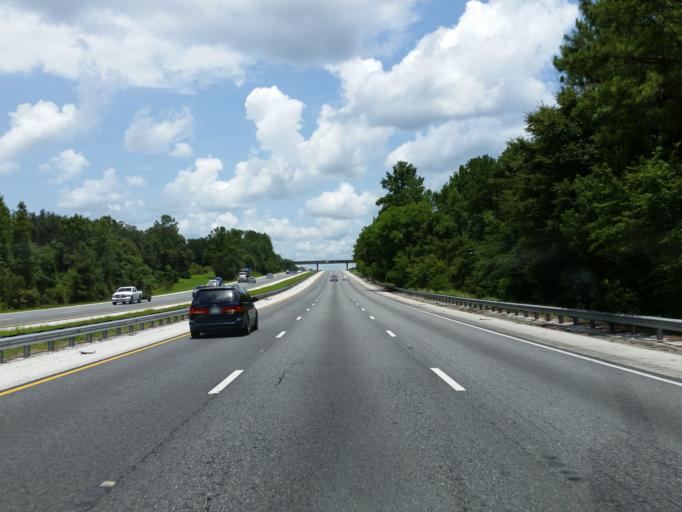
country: US
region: Florida
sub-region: Marion County
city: Citra
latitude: 29.4408
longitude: -82.2655
